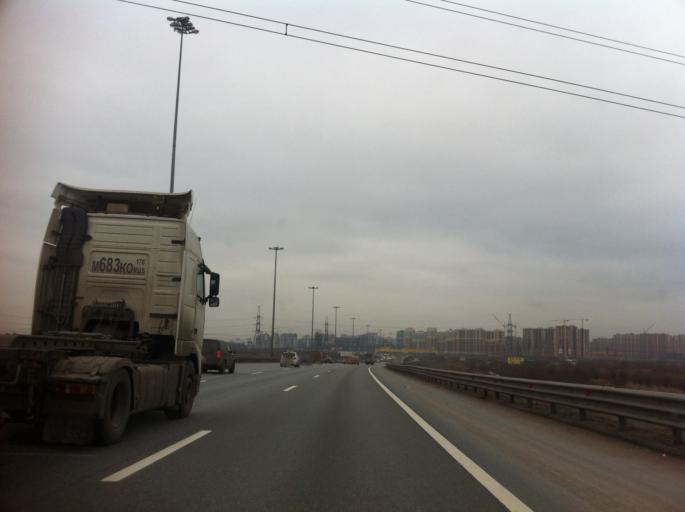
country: RU
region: St.-Petersburg
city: Krasnogvargeisky
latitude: 59.9299
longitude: 30.5352
